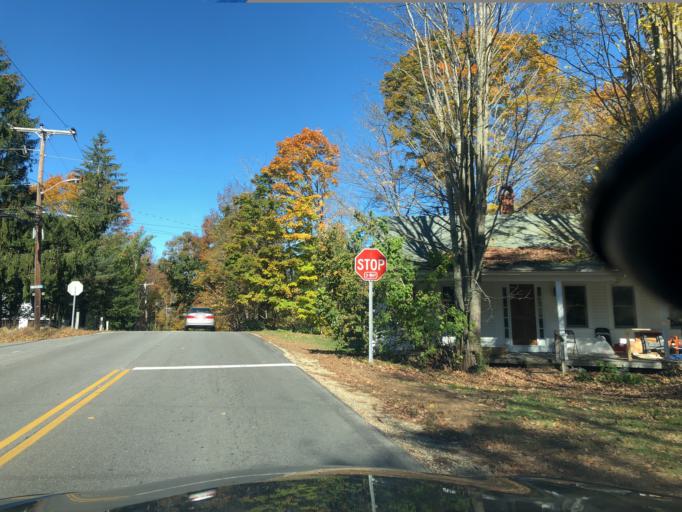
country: US
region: New Hampshire
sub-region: Rockingham County
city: Newmarket
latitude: 43.1066
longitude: -70.9558
